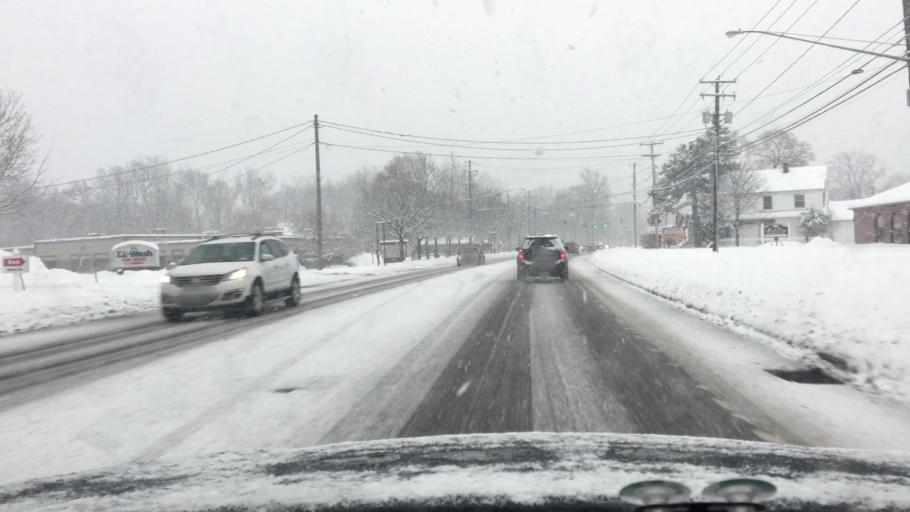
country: US
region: New York
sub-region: Erie County
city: Orchard Park
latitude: 42.7832
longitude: -78.7470
